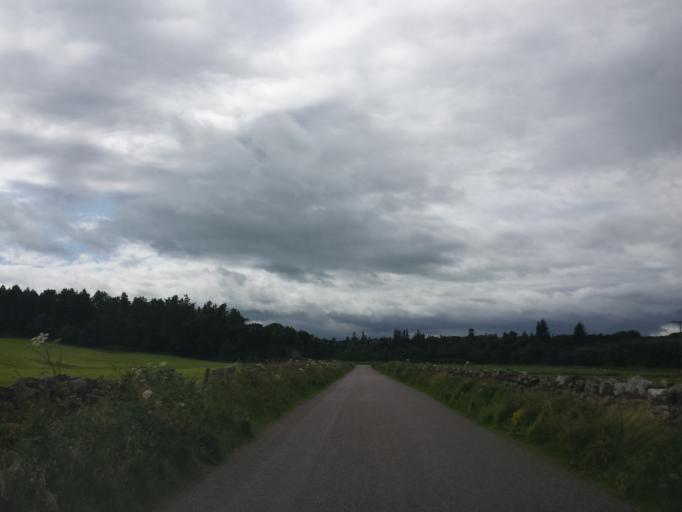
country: GB
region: Scotland
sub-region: Highland
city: Nairn
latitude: 57.5219
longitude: -3.9669
